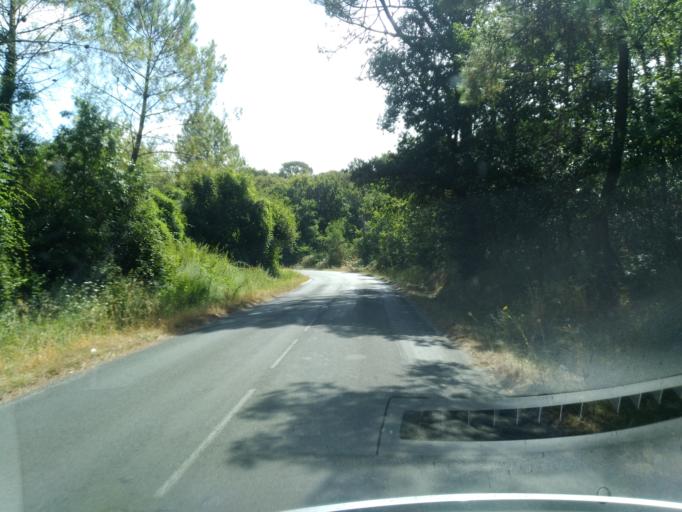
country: FR
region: Poitou-Charentes
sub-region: Departement de la Charente-Maritime
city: Saint-Palais-sur-Mer
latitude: 45.6654
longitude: -1.0781
